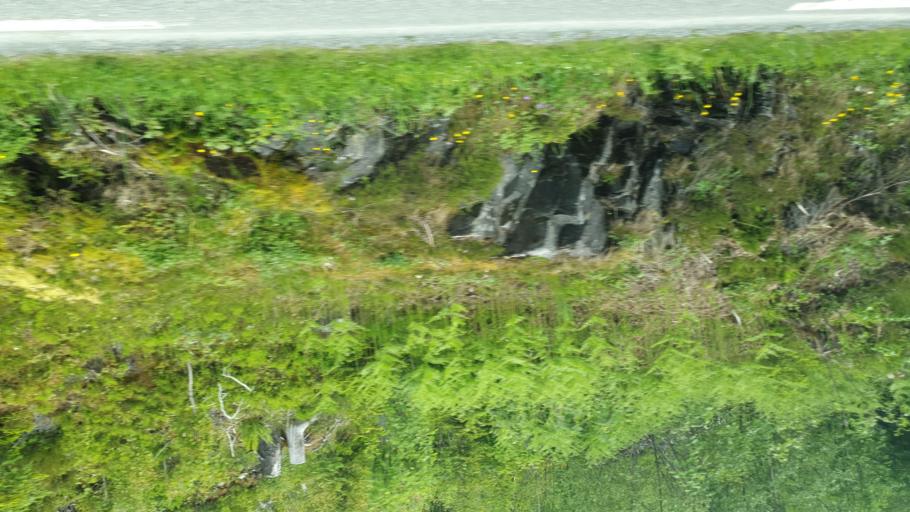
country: NO
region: Nord-Trondelag
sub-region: Leksvik
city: Leksvik
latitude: 63.6521
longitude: 10.6084
